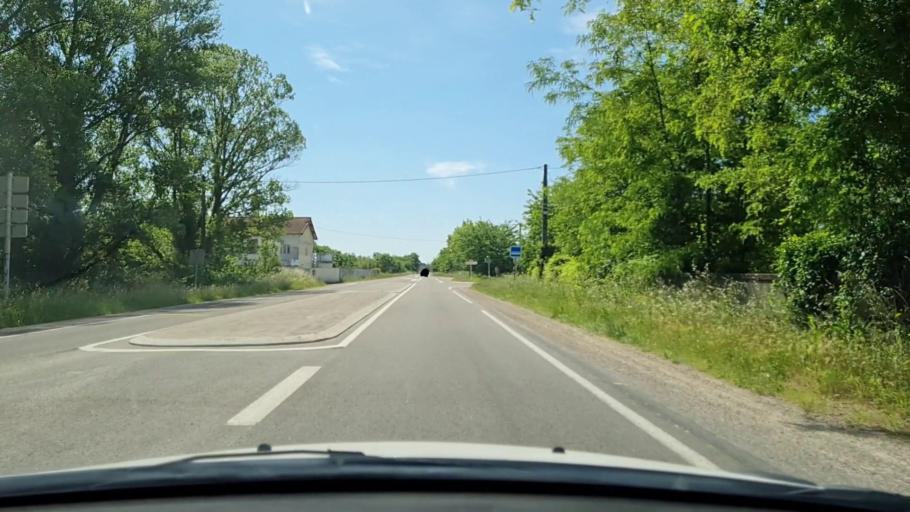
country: FR
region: Languedoc-Roussillon
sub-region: Departement du Gard
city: Moussac
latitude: 43.9693
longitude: 4.2230
